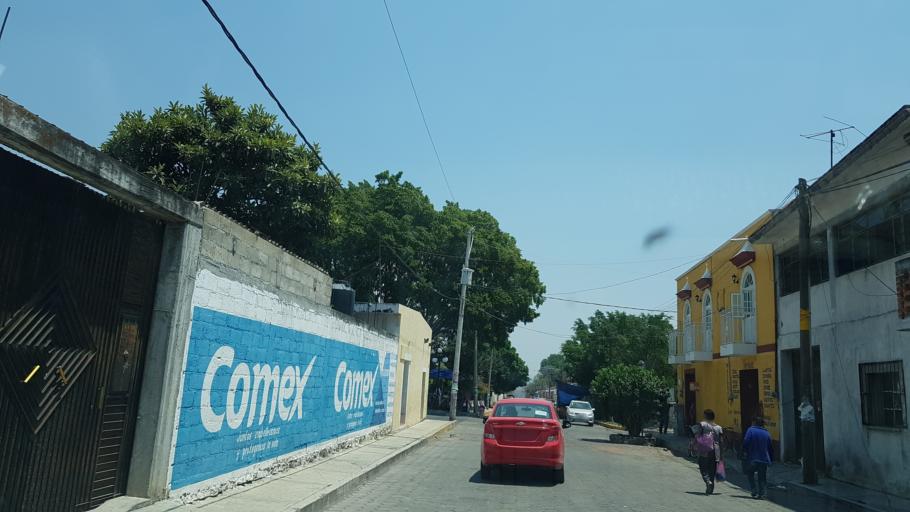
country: MX
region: Puebla
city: Huaquechula
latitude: 18.7689
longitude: -98.5420
